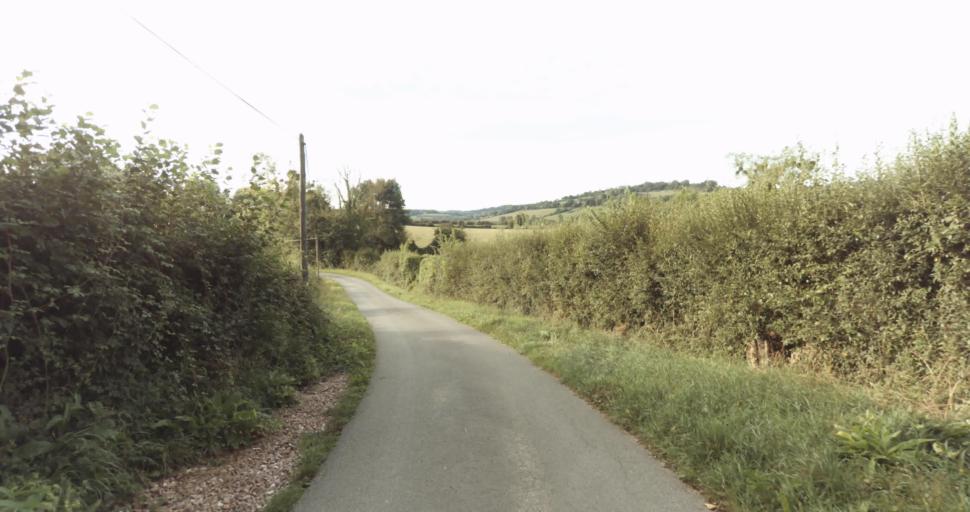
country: FR
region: Lower Normandy
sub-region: Departement de l'Orne
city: Vimoutiers
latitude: 48.8813
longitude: 0.2242
